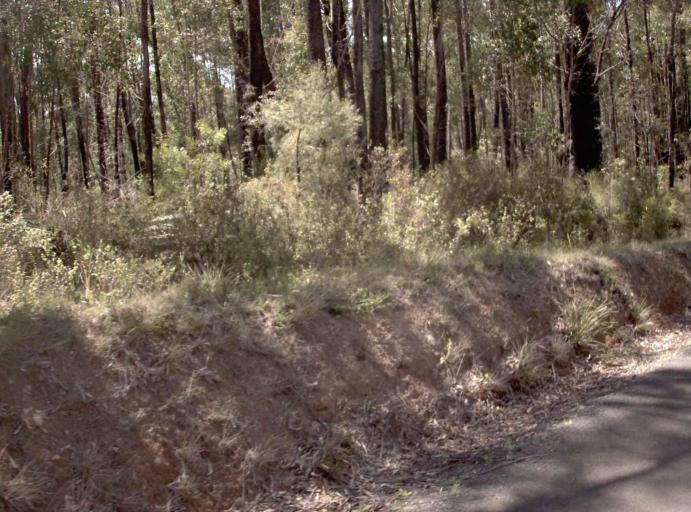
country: AU
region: New South Wales
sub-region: Bombala
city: Bombala
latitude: -37.5674
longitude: 149.0352
